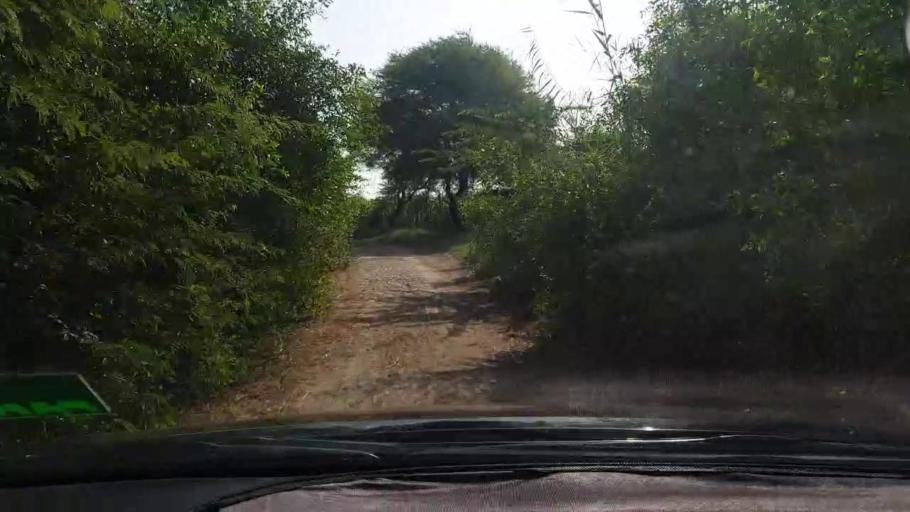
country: PK
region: Sindh
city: Tando Bago
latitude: 24.7148
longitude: 68.9898
